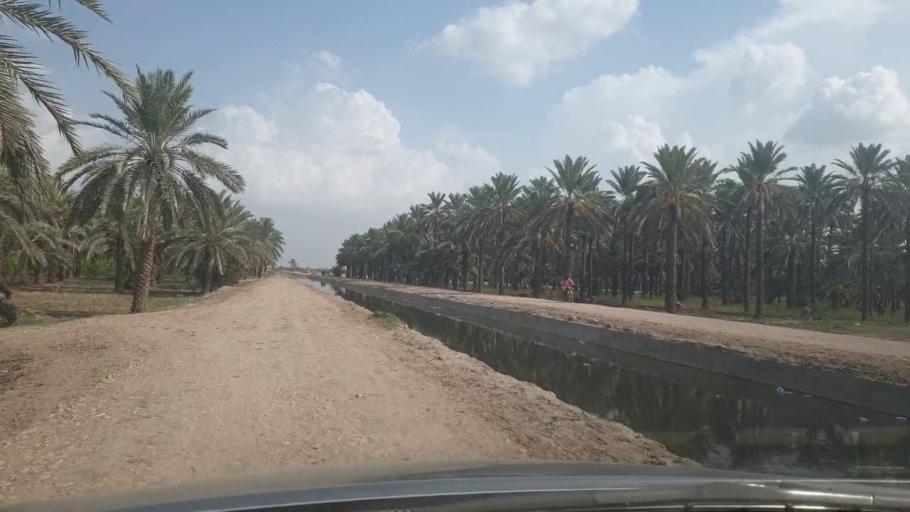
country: PK
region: Sindh
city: Khairpur
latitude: 27.5349
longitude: 68.7755
